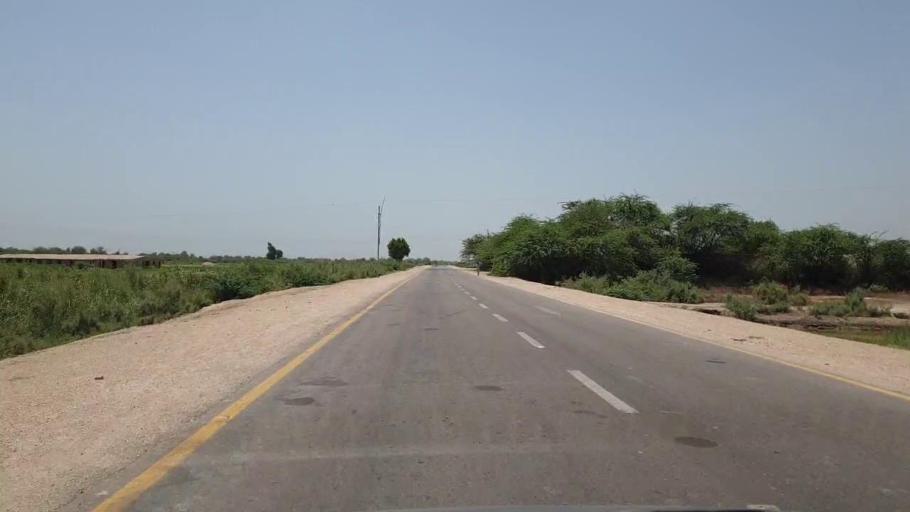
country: PK
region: Sindh
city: Sakrand
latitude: 26.1231
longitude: 68.3827
